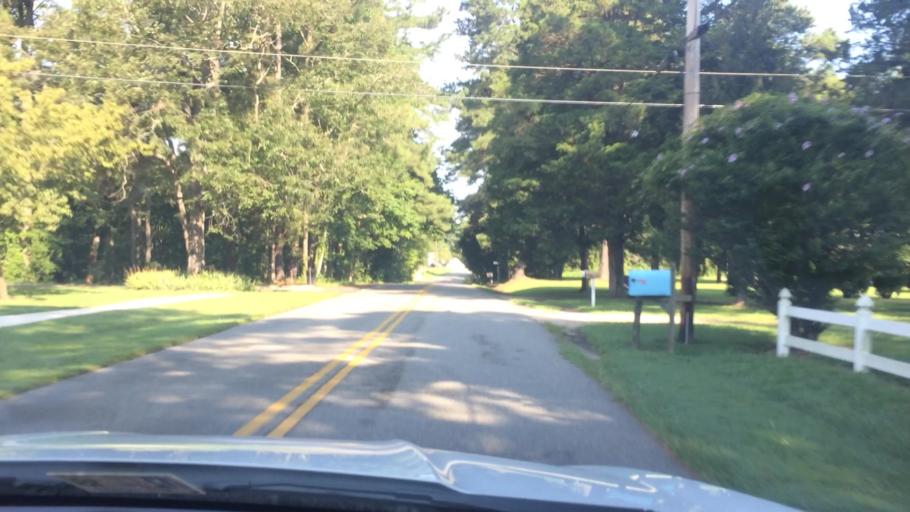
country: US
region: Virginia
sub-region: King William County
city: West Point
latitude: 37.5647
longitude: -76.8001
